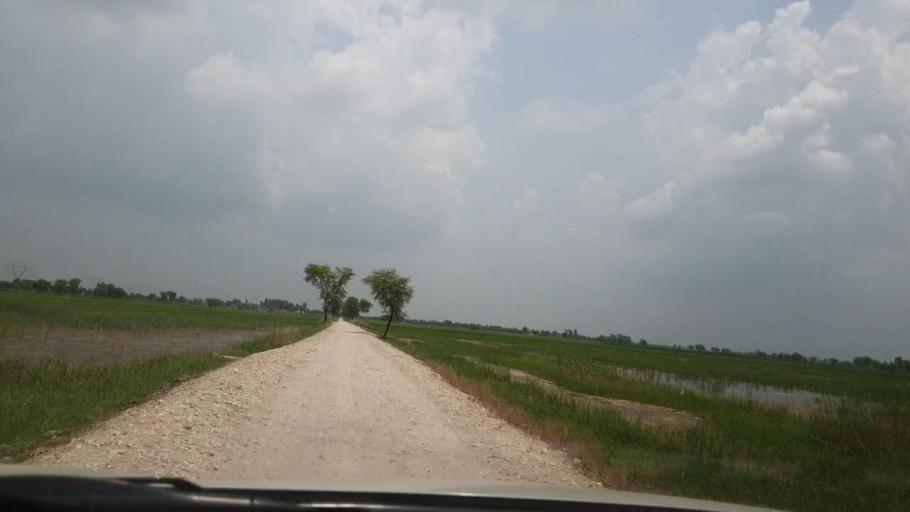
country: PK
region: Sindh
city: Goth Garelo
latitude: 27.4203
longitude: 68.0770
